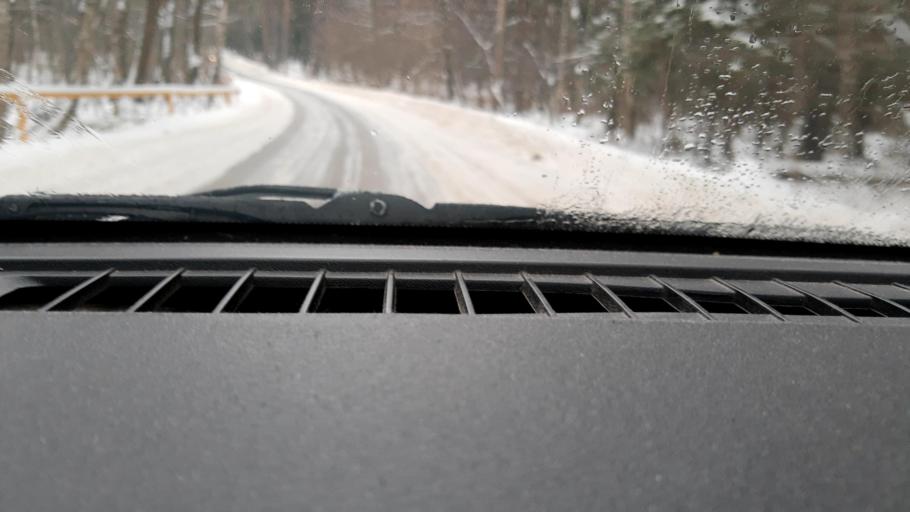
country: RU
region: Nizjnij Novgorod
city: Afonino
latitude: 56.1802
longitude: 44.0798
